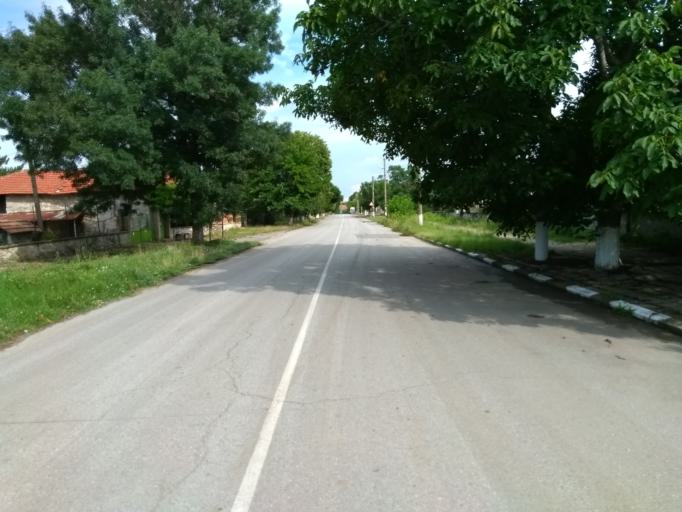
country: BG
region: Sliven
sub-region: Obshtina Sliven
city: Kermen
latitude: 42.4592
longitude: 26.1409
